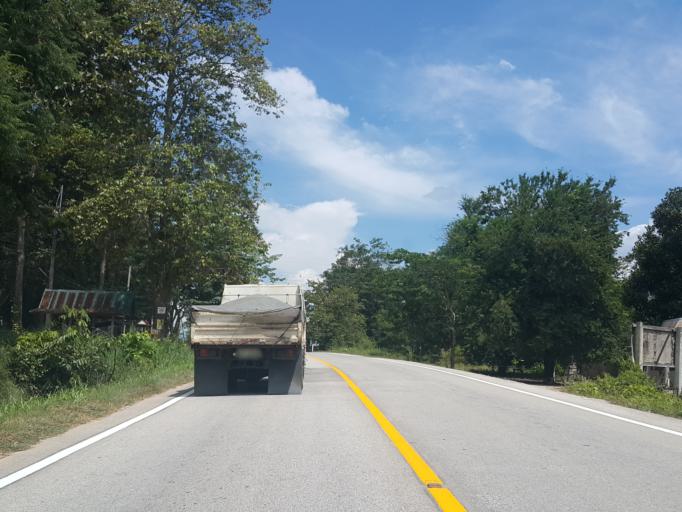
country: TH
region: Chiang Mai
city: Phrao
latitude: 19.2745
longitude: 99.1891
